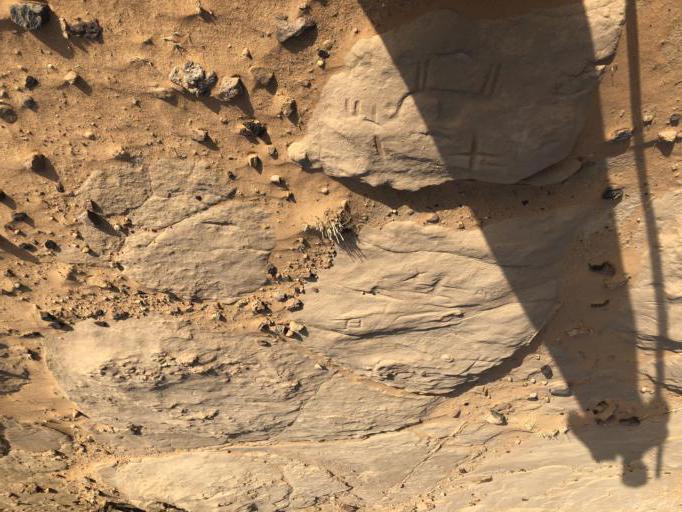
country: SA
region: Ar Riyad
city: shokhaib
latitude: 23.6283
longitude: 46.0844
